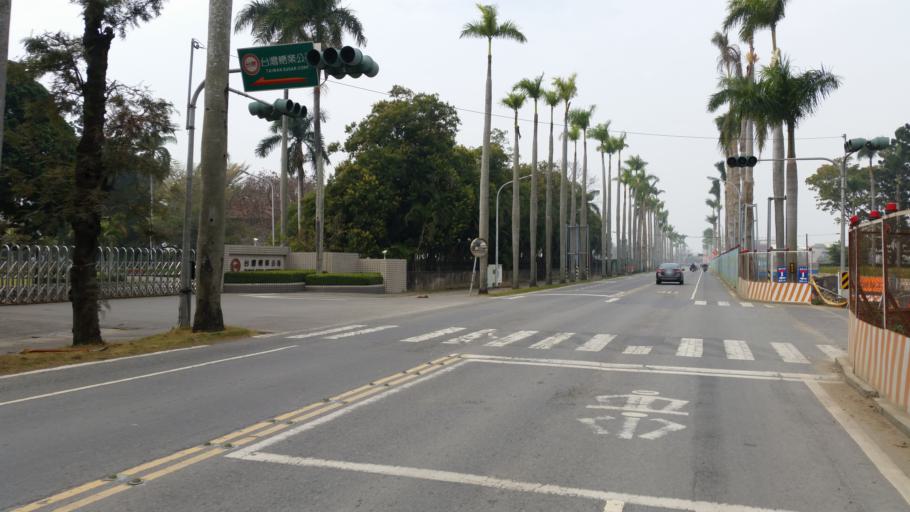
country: TW
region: Taiwan
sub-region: Tainan
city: Tainan
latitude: 22.9648
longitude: 120.2213
